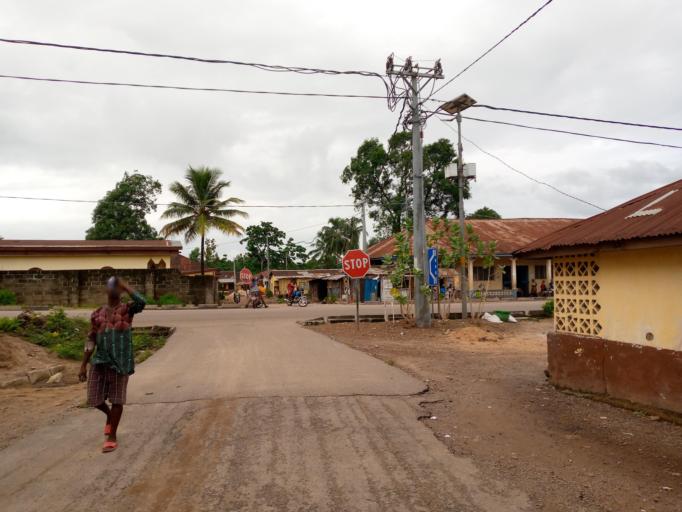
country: SL
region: Northern Province
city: Magburaka
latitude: 8.7228
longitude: -11.9471
